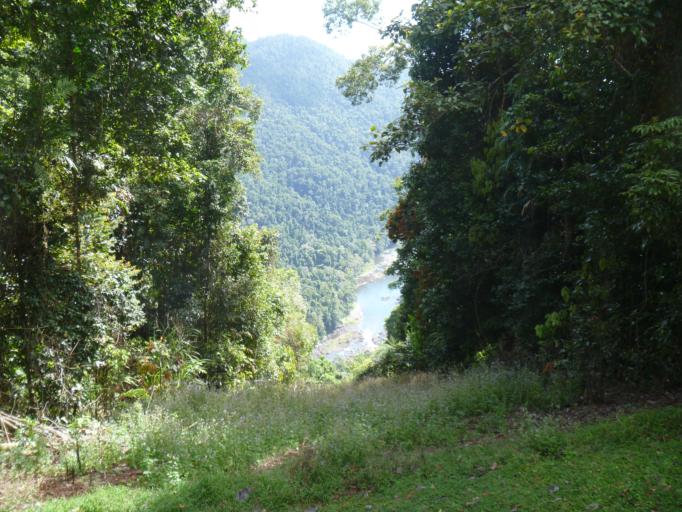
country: AU
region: Queensland
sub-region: Cassowary Coast
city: Innisfail
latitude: -17.6122
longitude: 145.7943
